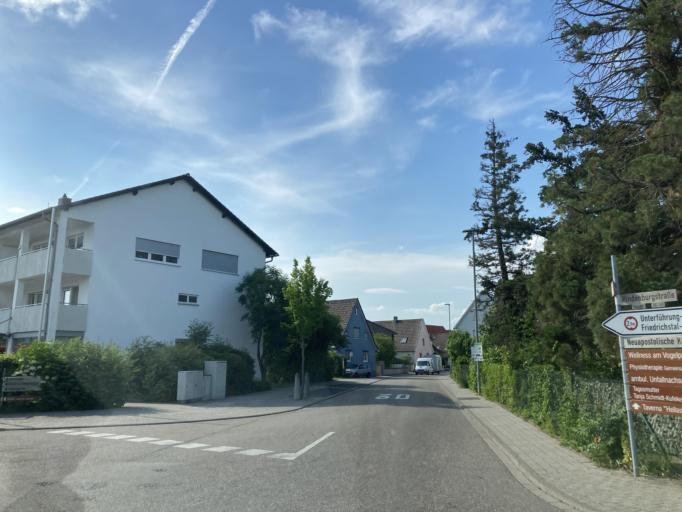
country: DE
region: Baden-Wuerttemberg
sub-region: Karlsruhe Region
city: Karlsdorf-Neuthard
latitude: 49.1040
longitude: 8.4819
